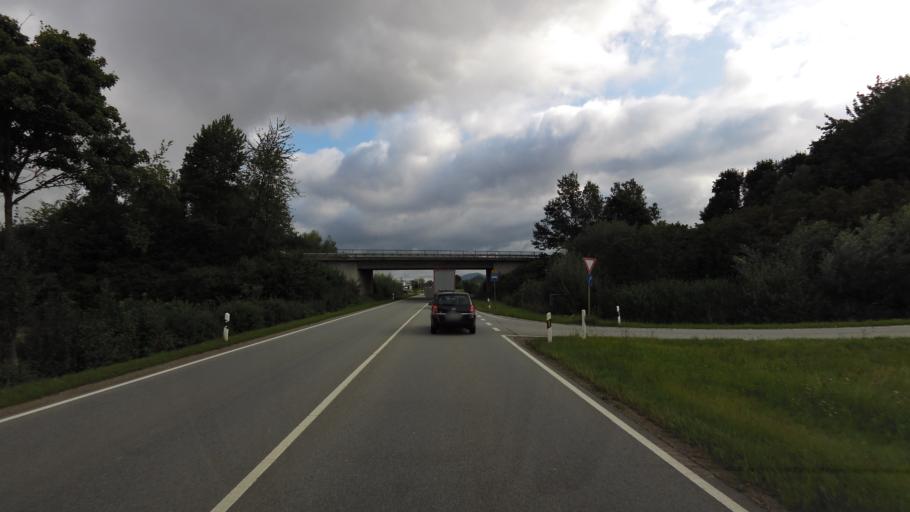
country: DE
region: Bavaria
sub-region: Lower Bavaria
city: Steinach
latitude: 48.9493
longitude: 12.6208
